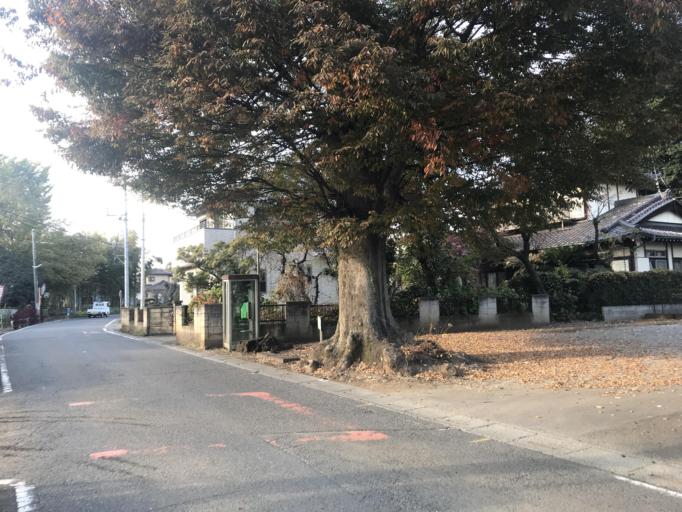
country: JP
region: Saitama
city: Tokorozawa
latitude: 35.8071
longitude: 139.5059
